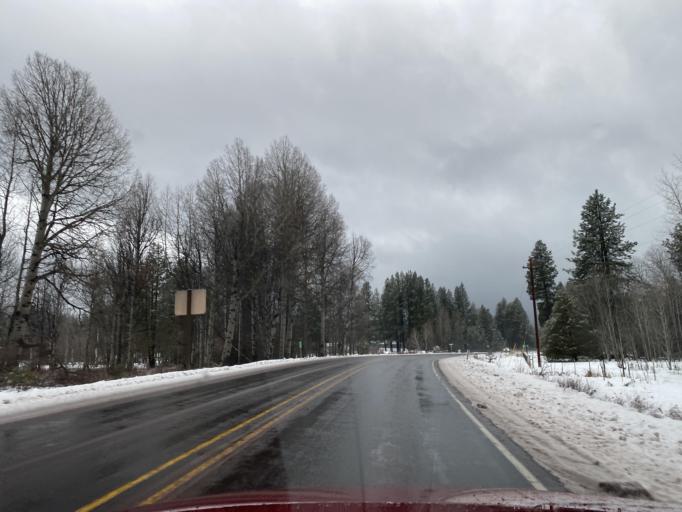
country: US
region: Oregon
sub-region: Klamath County
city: Klamath Falls
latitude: 42.4368
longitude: -122.1210
